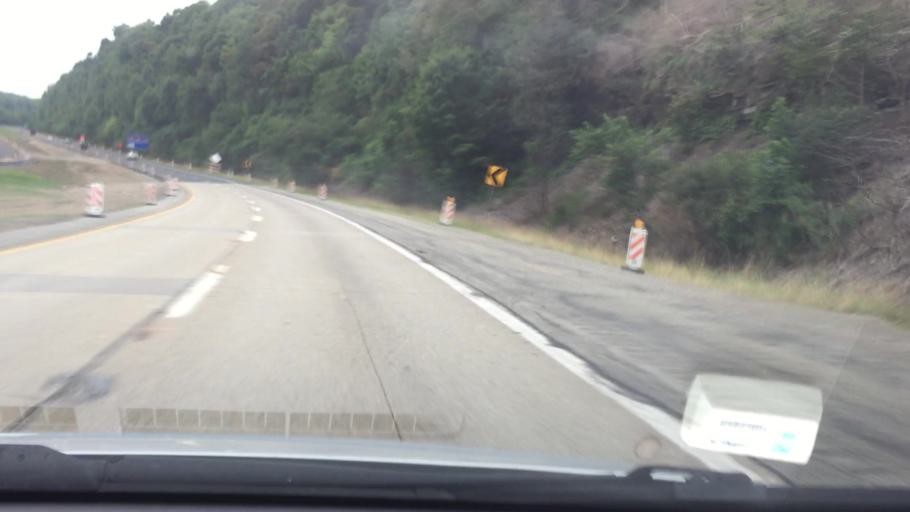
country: US
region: Pennsylvania
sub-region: Armstrong County
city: Freeport
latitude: 40.6531
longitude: -79.7250
